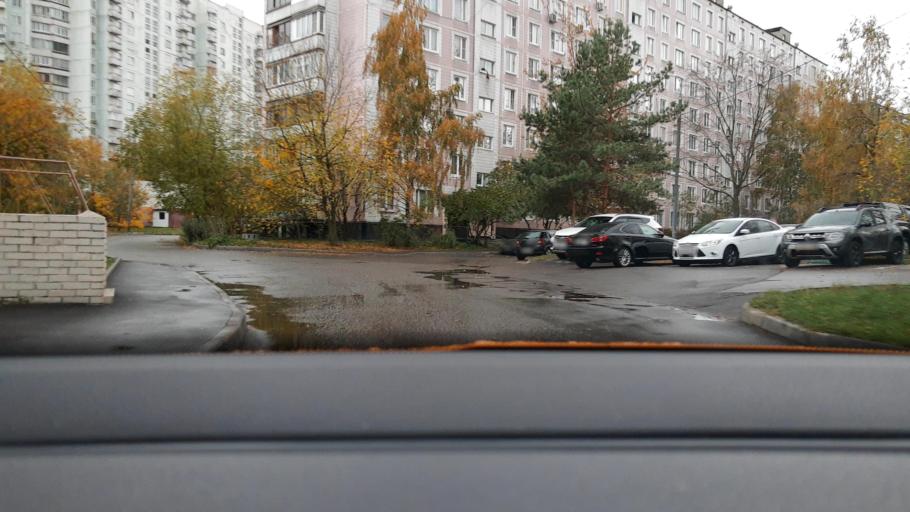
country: RU
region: Moscow
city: Strogino
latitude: 55.8138
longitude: 37.4031
